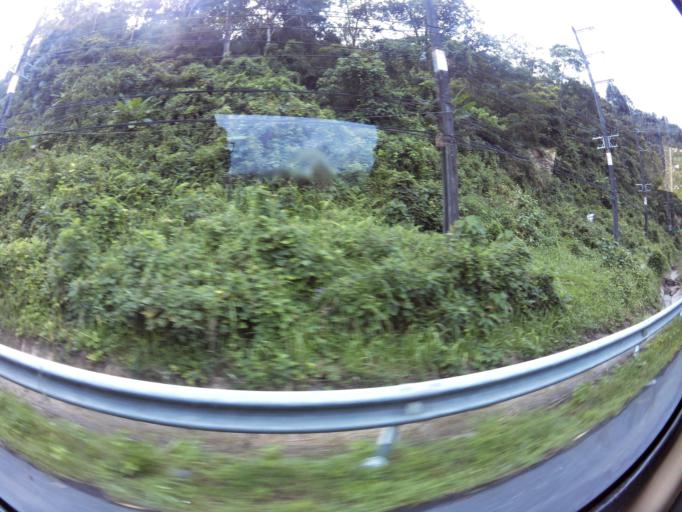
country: TH
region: Phuket
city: Patong
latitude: 7.9389
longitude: 98.2775
